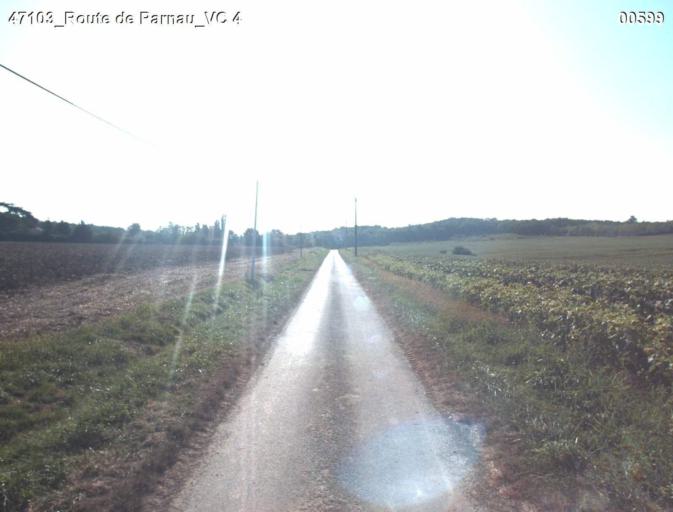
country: FR
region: Aquitaine
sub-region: Departement du Lot-et-Garonne
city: Nerac
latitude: 44.0824
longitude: 0.3360
